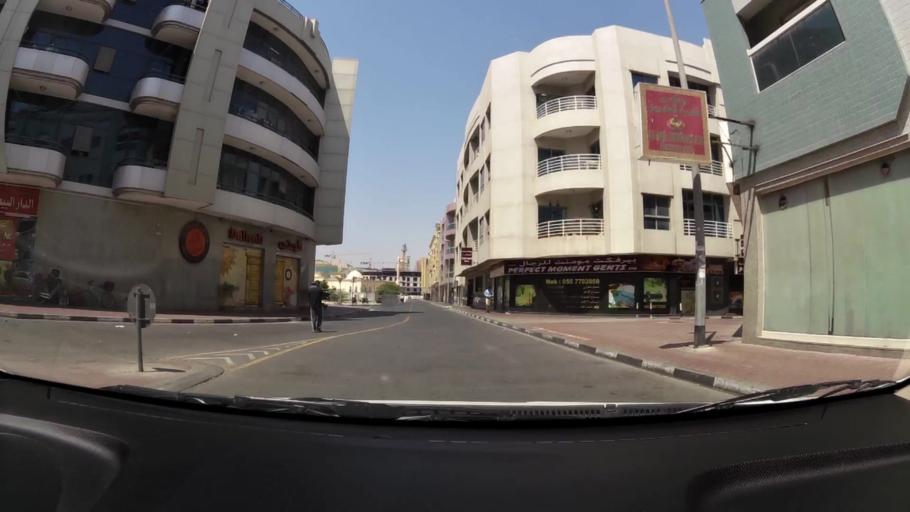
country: AE
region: Ash Shariqah
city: Sharjah
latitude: 25.2805
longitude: 55.3501
